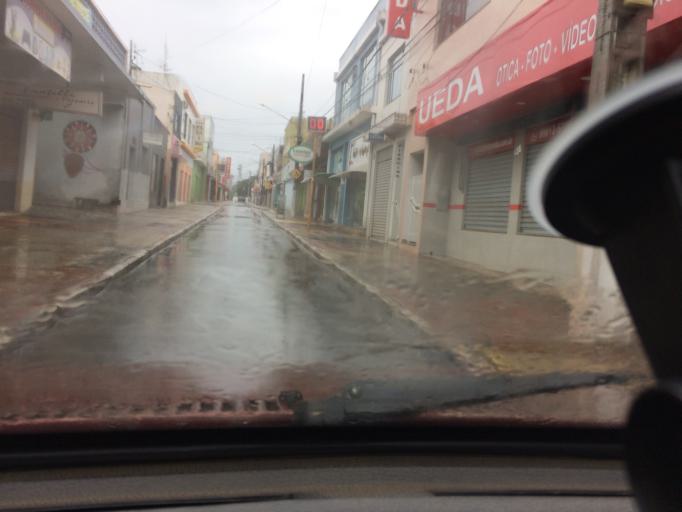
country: BR
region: Sao Paulo
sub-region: Capao Bonito
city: Capao Bonito
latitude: -24.0061
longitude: -48.3480
